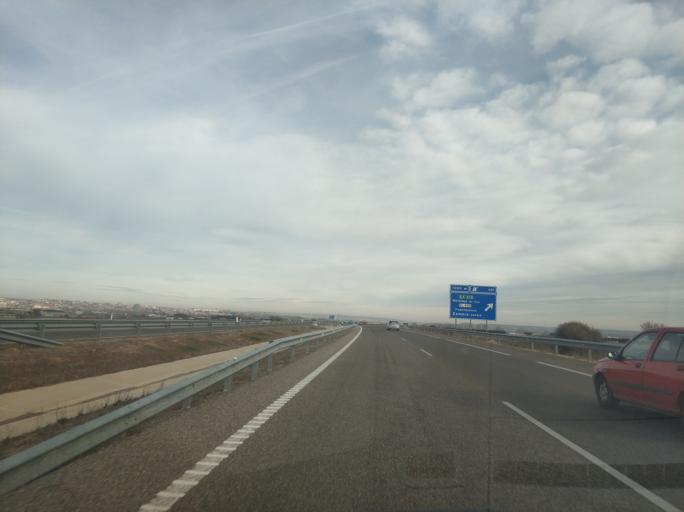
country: ES
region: Castille and Leon
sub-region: Provincia de Zamora
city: Morales del Vino
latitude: 41.4720
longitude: -5.7197
